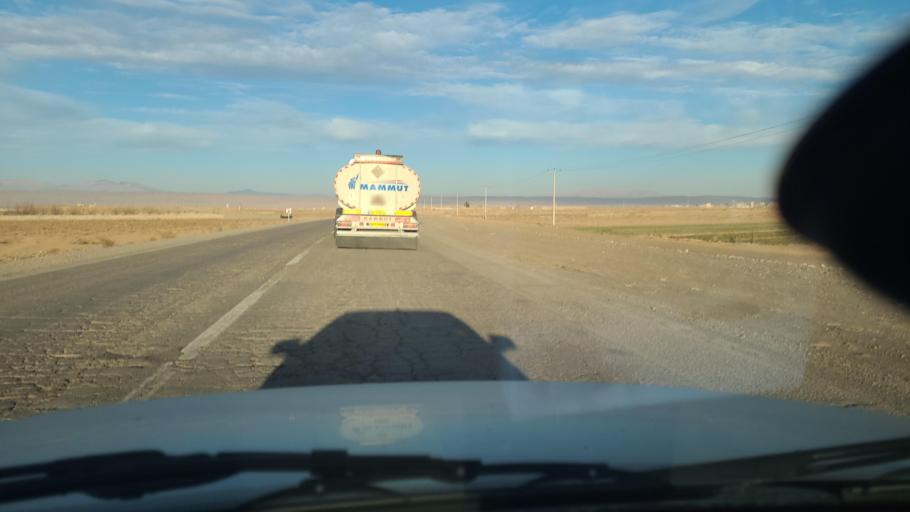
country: IR
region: Razavi Khorasan
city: Neqab
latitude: 36.6140
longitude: 57.5966
